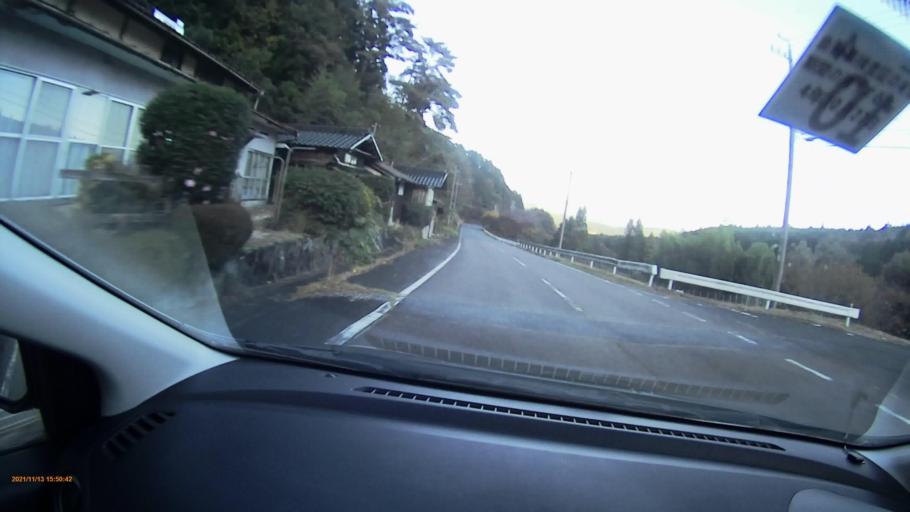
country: JP
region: Gifu
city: Nakatsugawa
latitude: 35.5967
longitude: 137.4139
